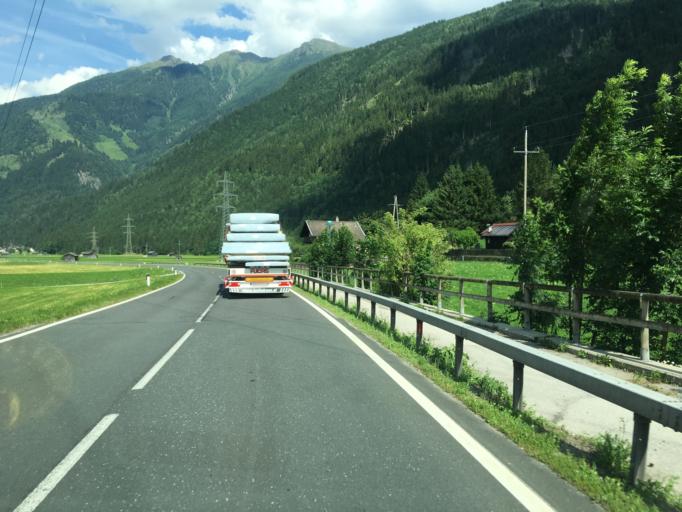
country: AT
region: Carinthia
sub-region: Politischer Bezirk Spittal an der Drau
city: Stall
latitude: 46.8881
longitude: 13.0451
